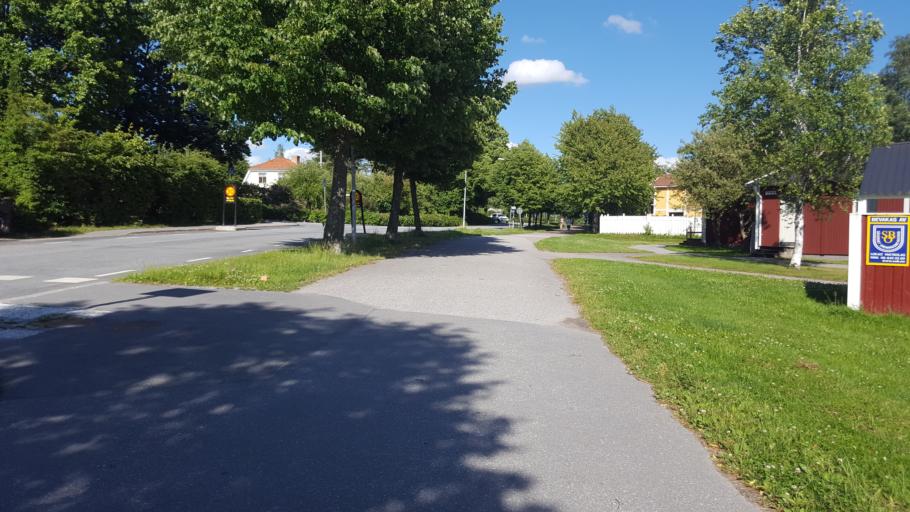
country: SE
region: Stockholm
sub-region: Upplands Vasby Kommun
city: Upplands Vaesby
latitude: 59.5170
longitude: 17.8891
